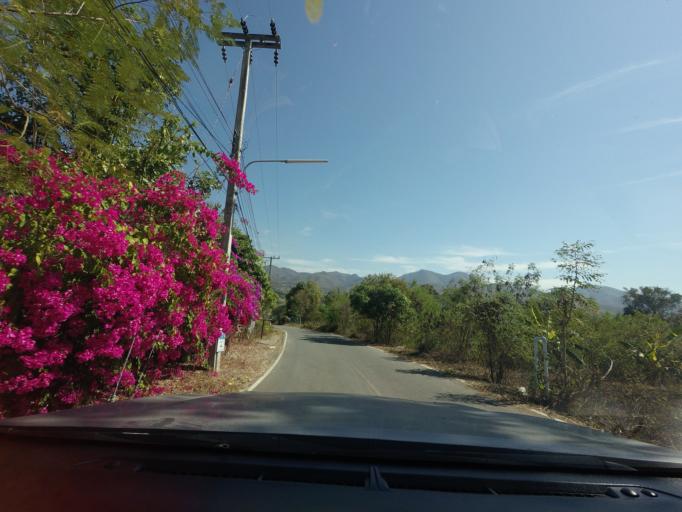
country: TH
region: Mae Hong Son
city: Wiang Nuea
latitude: 19.3858
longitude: 98.4374
